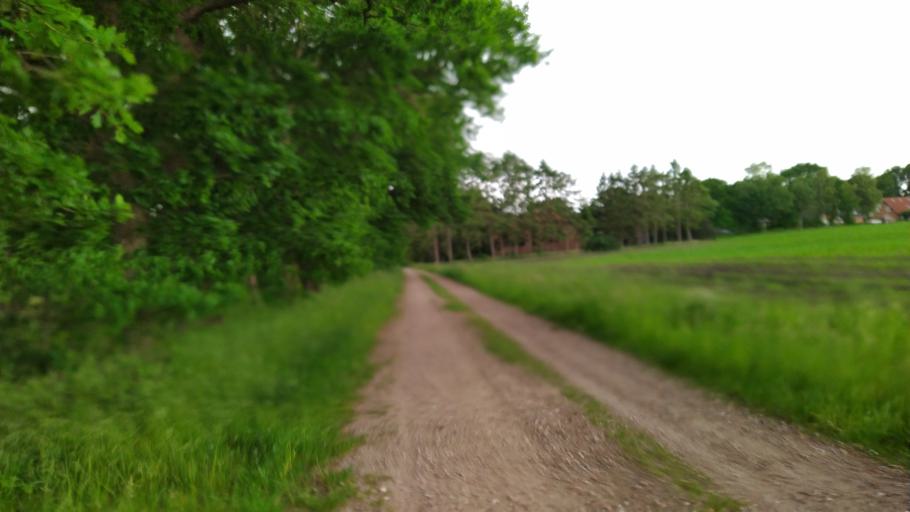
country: DE
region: Lower Saxony
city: Farven
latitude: 53.4306
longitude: 9.2747
